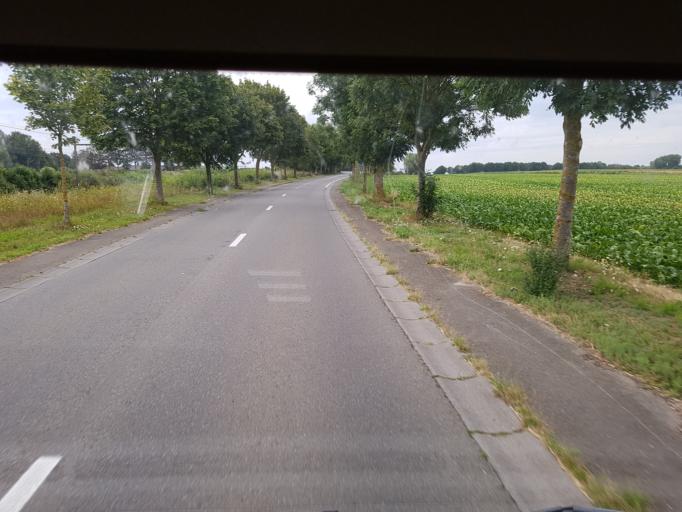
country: FR
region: Nord-Pas-de-Calais
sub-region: Departement du Nord
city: Flines-les-Mortagne
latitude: 50.5386
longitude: 3.5108
